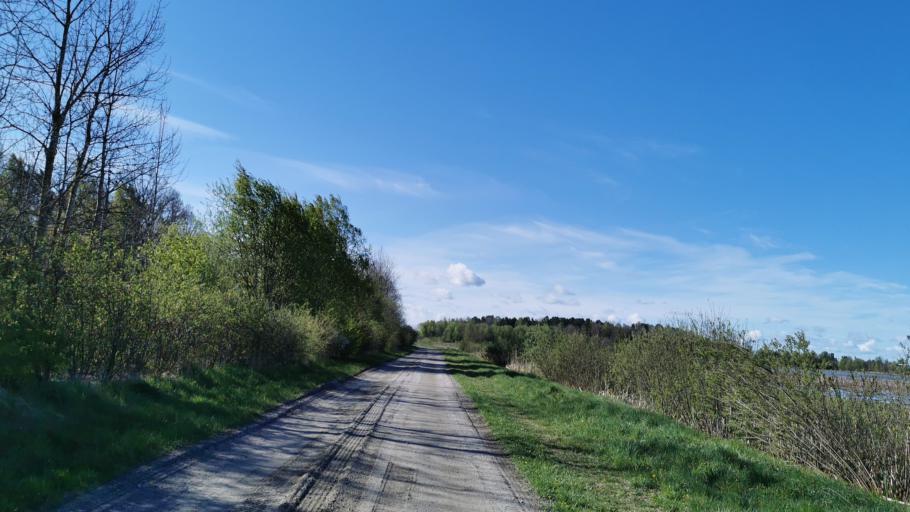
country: SE
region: OErebro
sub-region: Orebro Kommun
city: Orebro
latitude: 59.3031
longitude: 15.2208
